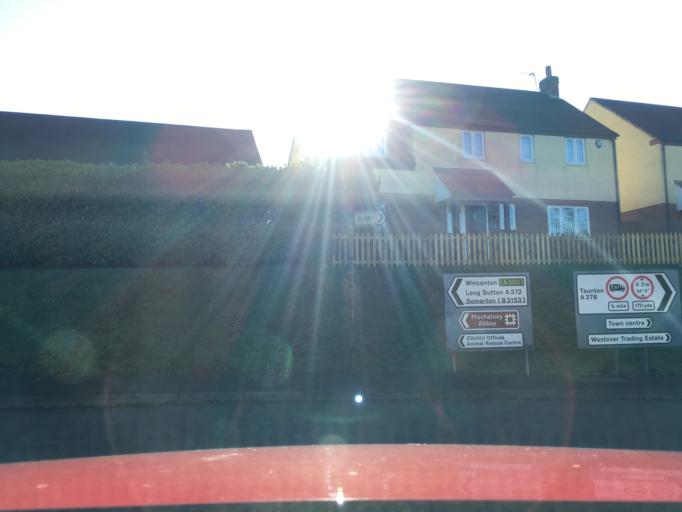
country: GB
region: England
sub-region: Somerset
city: Langport
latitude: 51.0421
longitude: -2.8243
